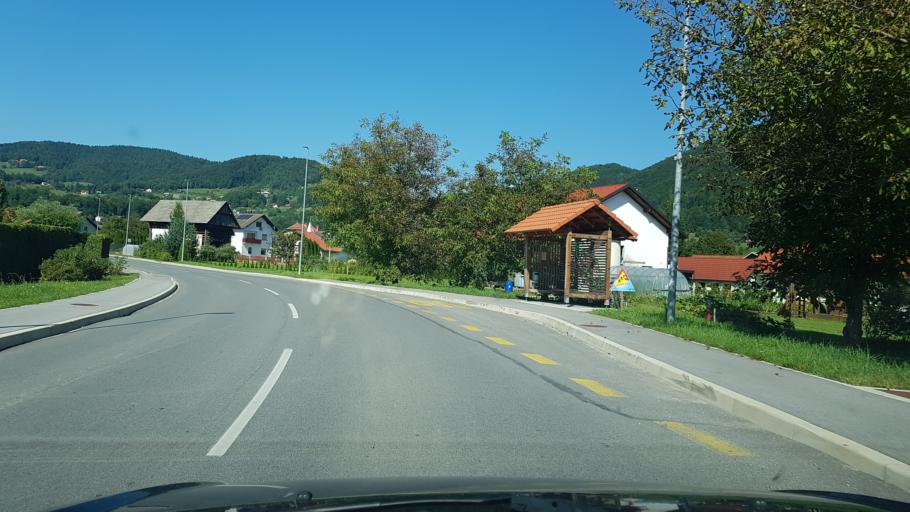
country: SI
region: Smartno ob Paki
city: Smartno ob Paki
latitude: 46.3218
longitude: 15.0393
